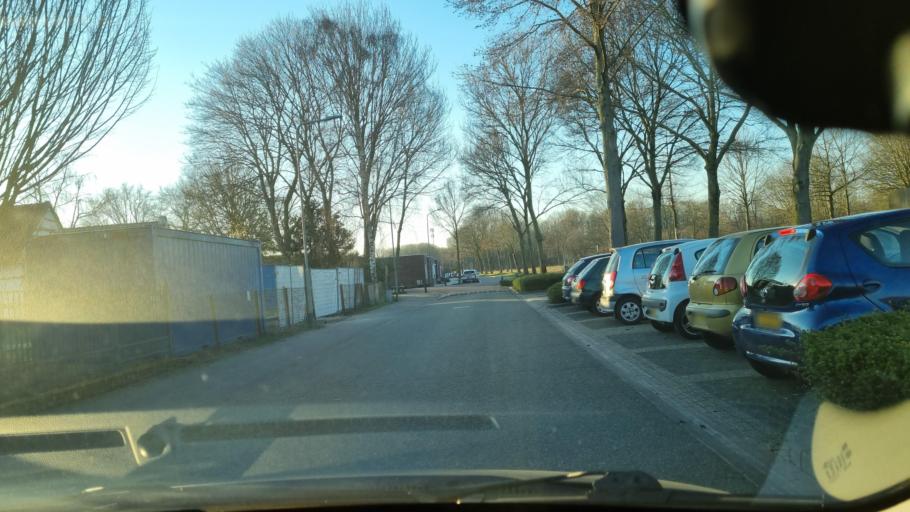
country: NL
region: Limburg
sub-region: Gemeente Sittard-Geleen
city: Sittard
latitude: 51.0051
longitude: 5.8934
